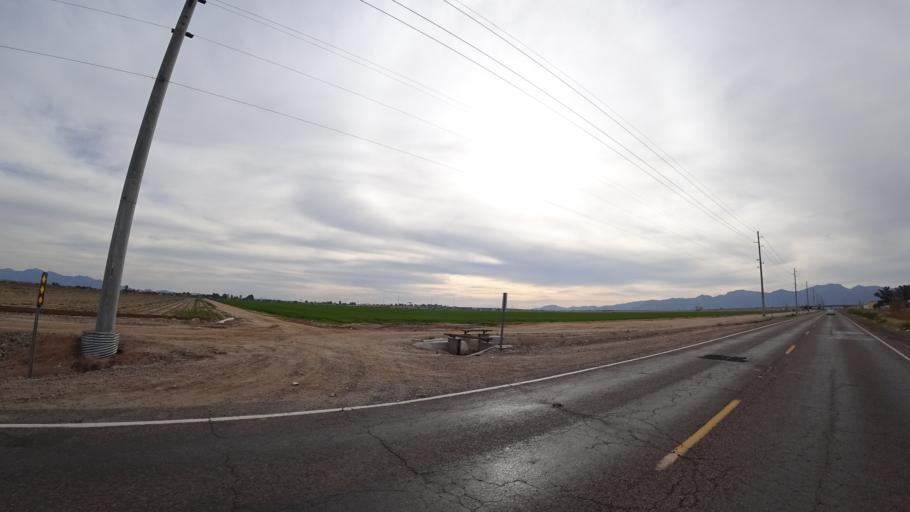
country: US
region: Arizona
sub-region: Maricopa County
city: Citrus Park
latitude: 33.5662
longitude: -112.4020
